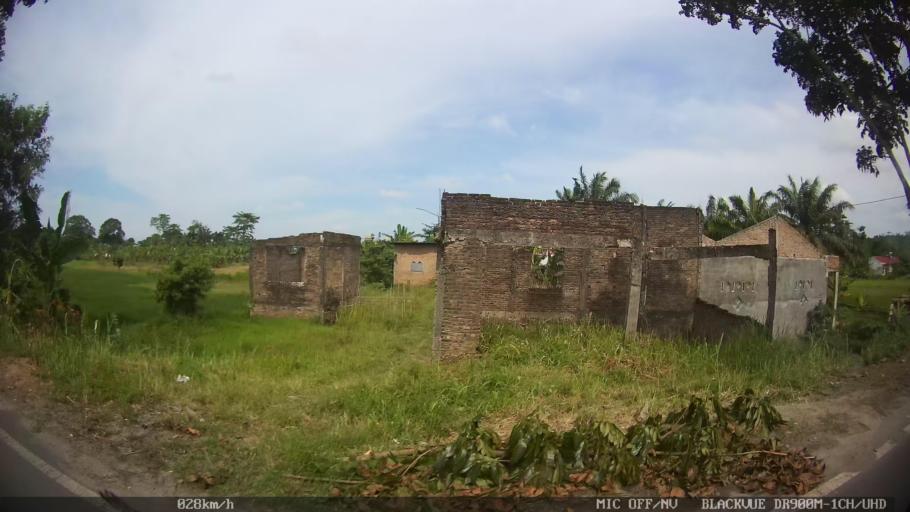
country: ID
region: North Sumatra
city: Percut
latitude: 3.6124
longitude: 98.8309
